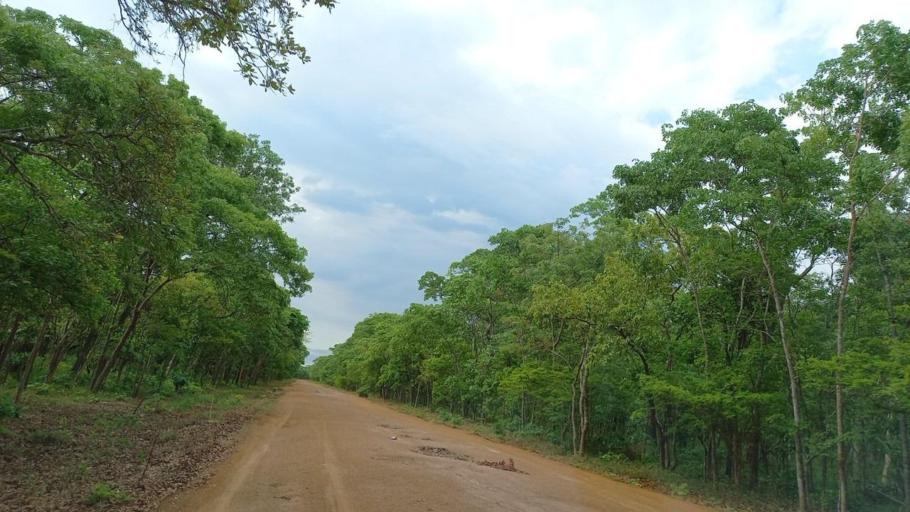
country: ZM
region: North-Western
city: Kalengwa
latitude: -13.3860
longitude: 25.0712
